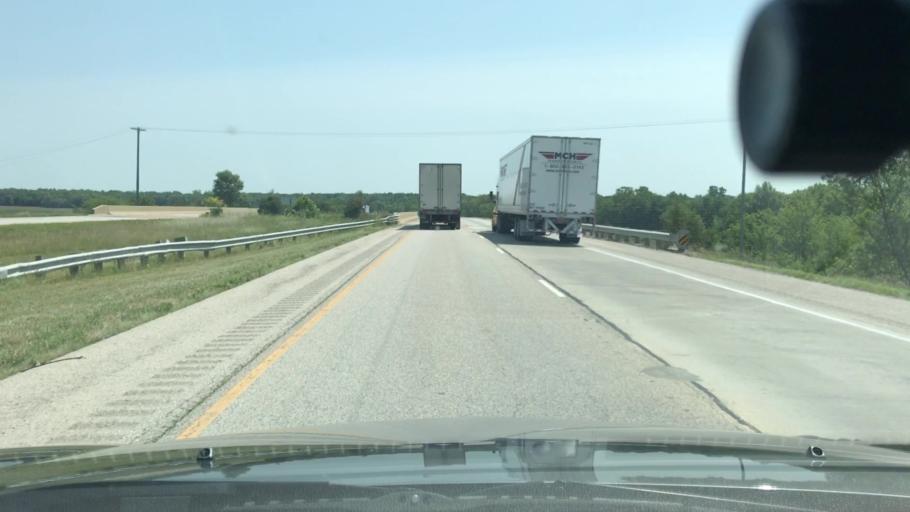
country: US
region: Illinois
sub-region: Washington County
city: Nashville
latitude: 38.3903
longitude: -89.3370
